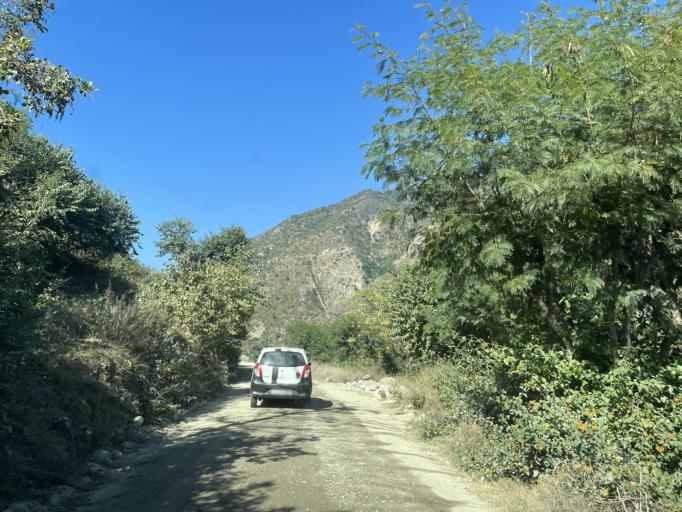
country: IN
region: Uttarakhand
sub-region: Almora
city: Ranikhet
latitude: 29.5530
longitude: 79.3972
